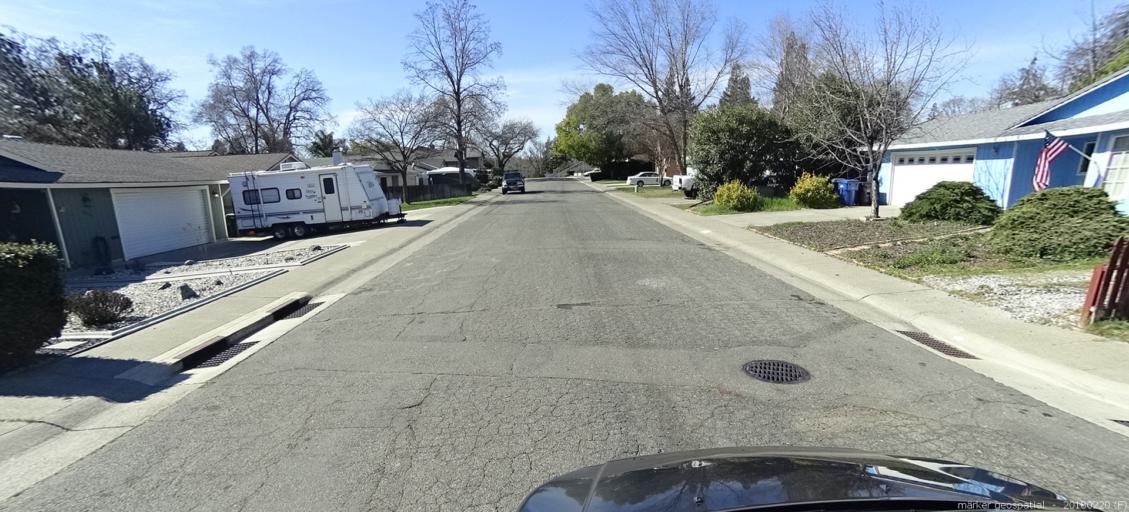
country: US
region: California
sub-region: Sacramento County
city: Orangevale
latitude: 38.6810
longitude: -121.2364
